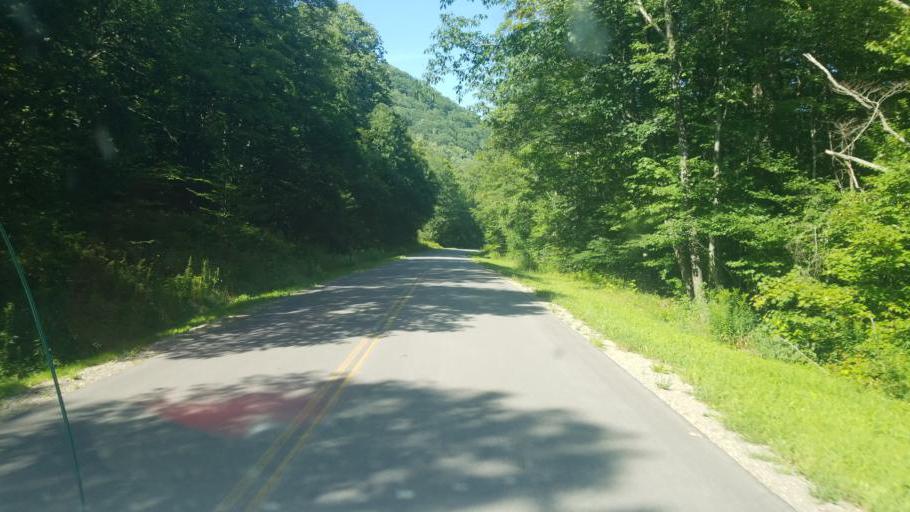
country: US
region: New York
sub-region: Allegany County
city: Wellsville
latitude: 42.0179
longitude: -77.9870
